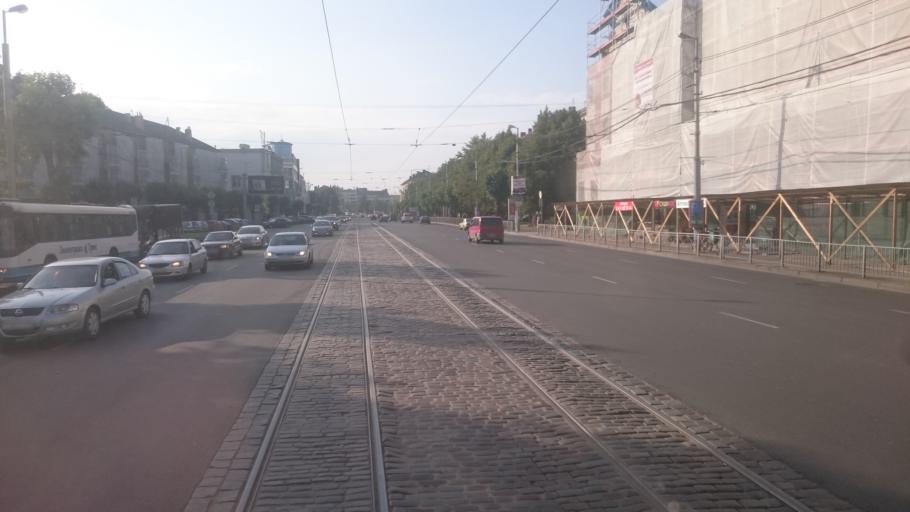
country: RU
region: Kaliningrad
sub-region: Gorod Kaliningrad
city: Kaliningrad
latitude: 54.7128
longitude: 20.5075
